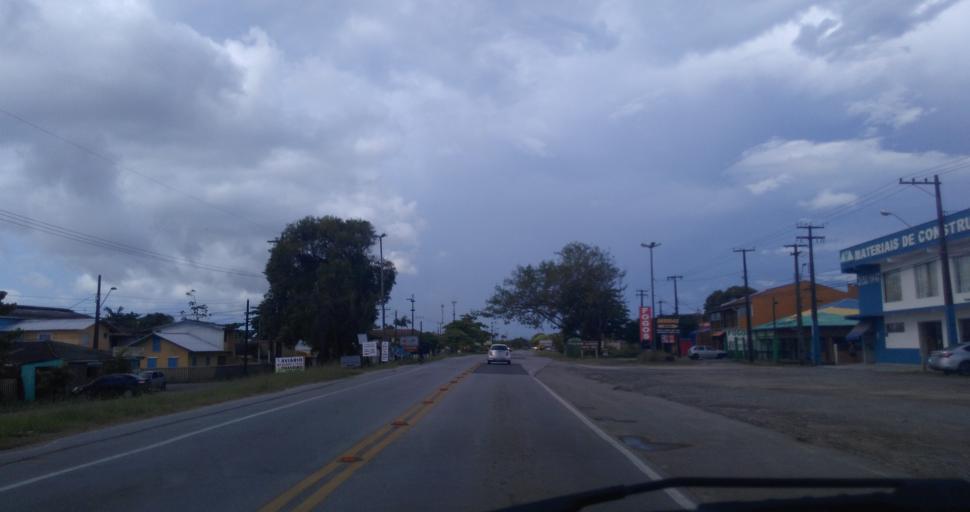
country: BR
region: Parana
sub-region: Pontal Do Parana
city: Pontal do Parana
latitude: -25.7373
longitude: -48.4948
